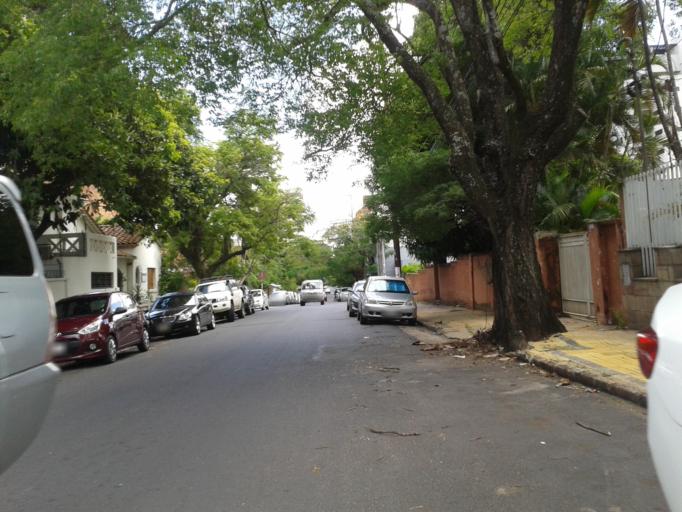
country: PY
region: Asuncion
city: Asuncion
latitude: -25.2941
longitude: -57.6163
